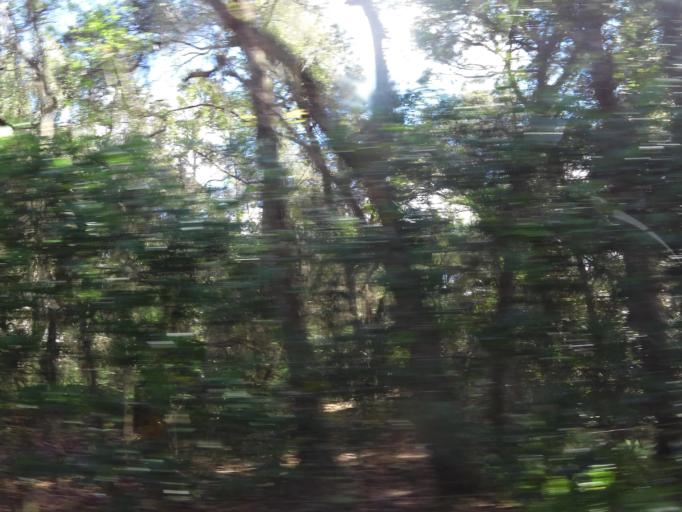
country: US
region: Florida
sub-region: Volusia County
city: Orange City
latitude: 28.9493
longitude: -81.3155
